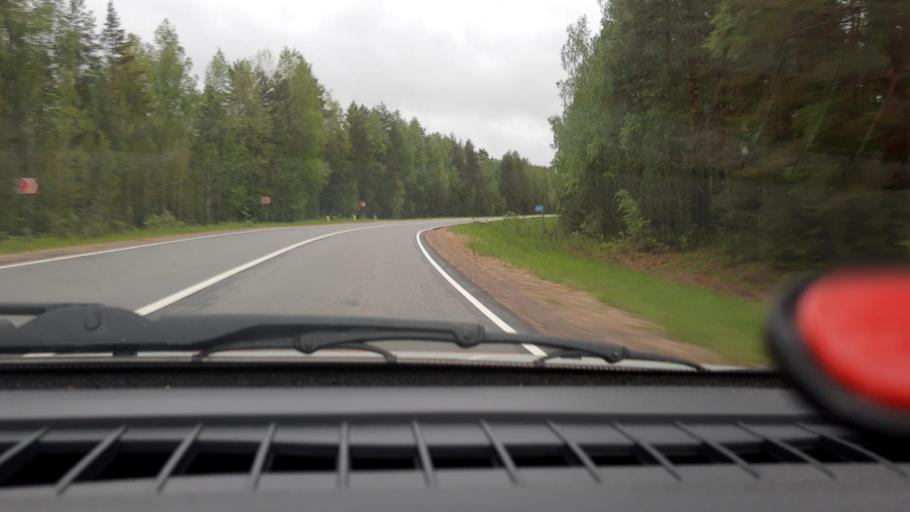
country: RU
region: Nizjnij Novgorod
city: Krasnyye Baki
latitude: 57.2124
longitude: 45.4630
